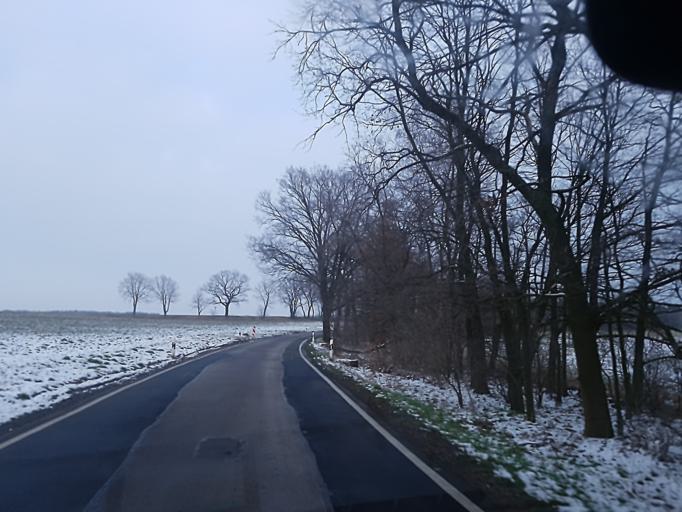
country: DE
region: Saxony
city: Cavertitz
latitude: 51.3916
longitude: 13.1640
